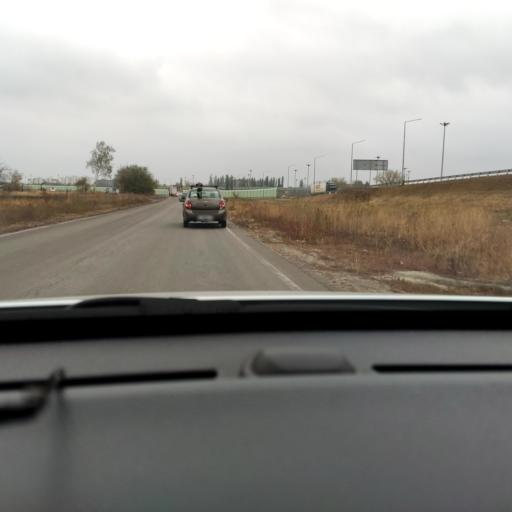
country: RU
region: Voronezj
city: Novaya Usman'
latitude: 51.6539
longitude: 39.3041
